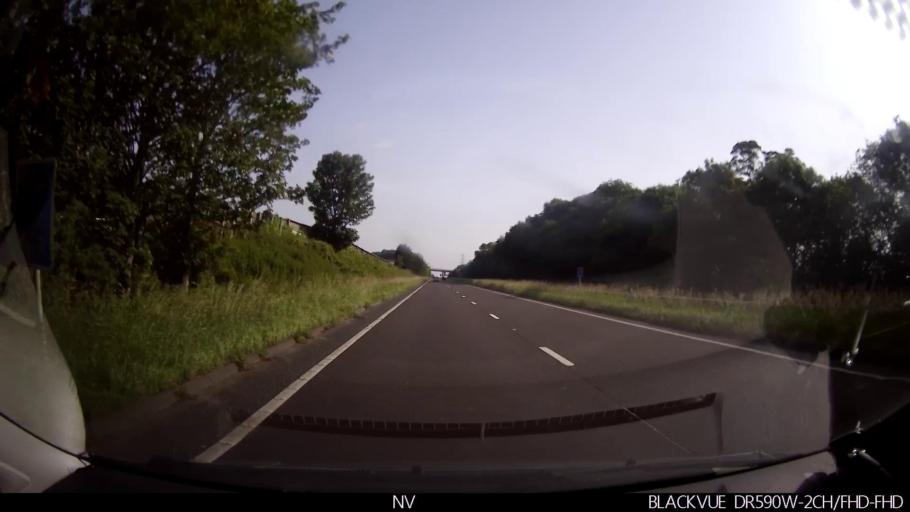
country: GB
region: England
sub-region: North Yorkshire
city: Malton
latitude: 54.1287
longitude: -0.8235
